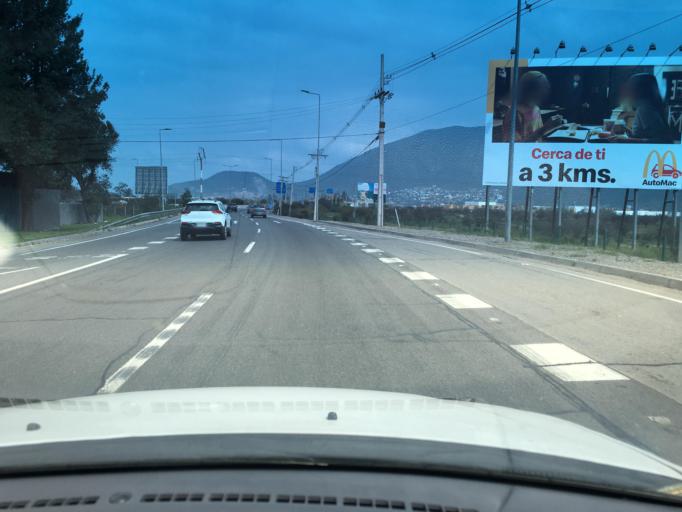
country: CL
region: Santiago Metropolitan
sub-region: Provincia de Santiago
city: Lo Prado
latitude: -33.4345
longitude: -70.8112
